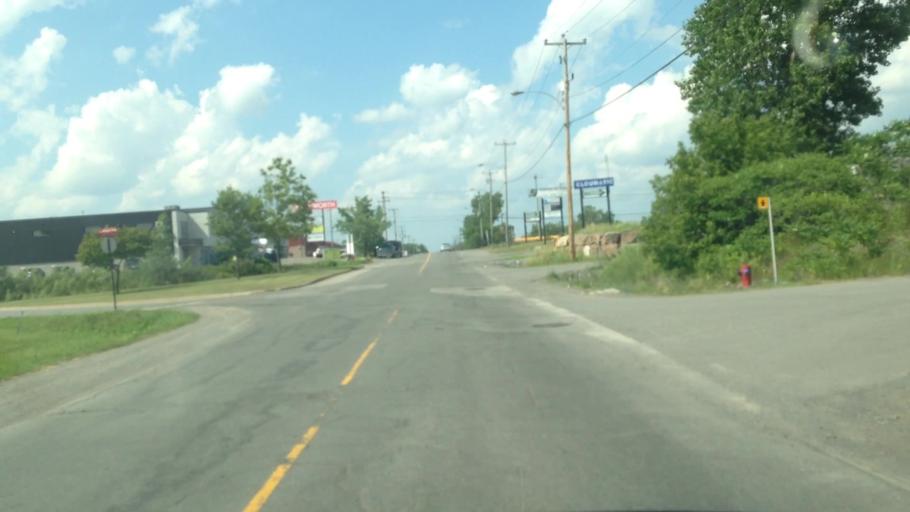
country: CA
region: Quebec
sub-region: Laurentides
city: Saint-Jerome
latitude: 45.7635
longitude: -74.0229
